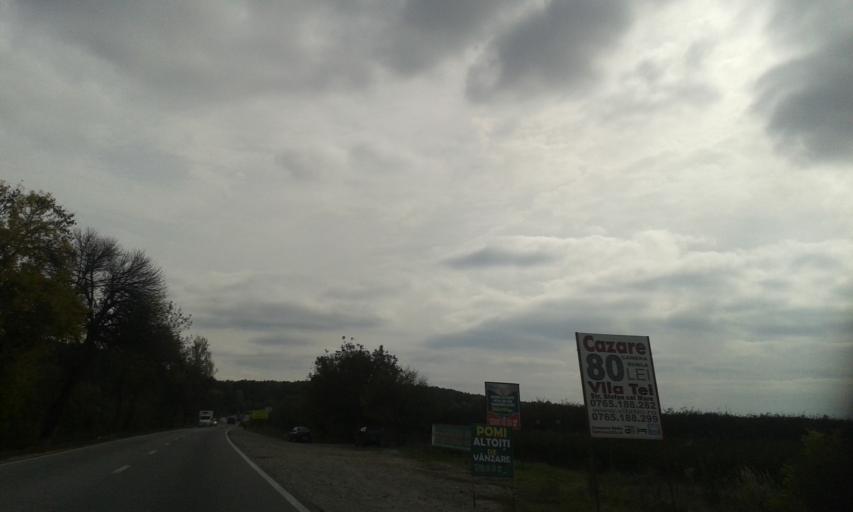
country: RO
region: Gorj
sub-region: Comuna Balanesti
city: Balanesti
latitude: 45.0364
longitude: 23.3727
